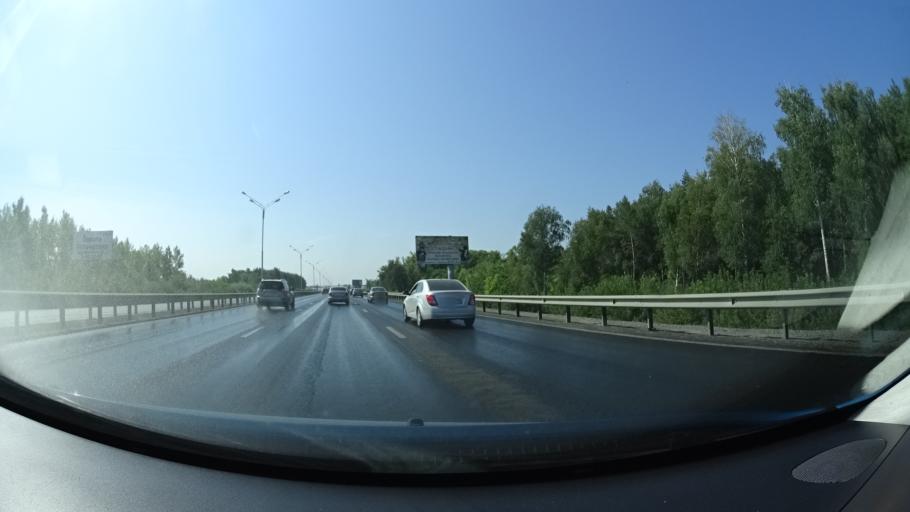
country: RU
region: Bashkortostan
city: Ufa
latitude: 54.6867
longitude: 55.9380
